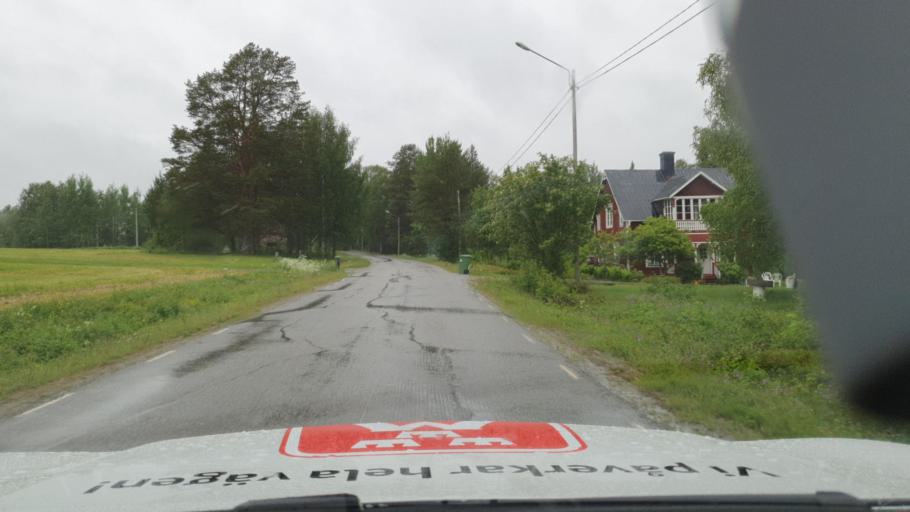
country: SE
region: Vaesterbotten
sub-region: Lycksele Kommun
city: Lycksele
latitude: 64.0747
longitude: 18.3636
